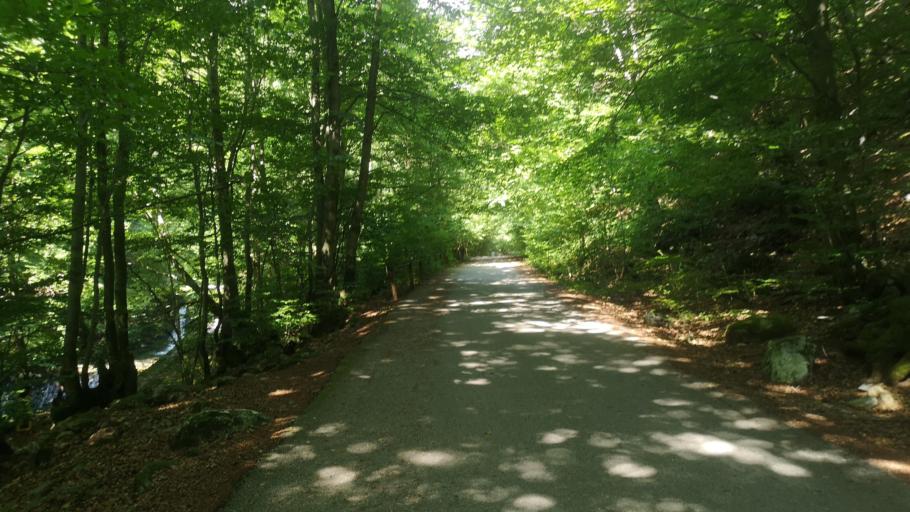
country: SK
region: Zilinsky
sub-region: Okres Zilina
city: Terchova
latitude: 49.1631
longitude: 19.0835
